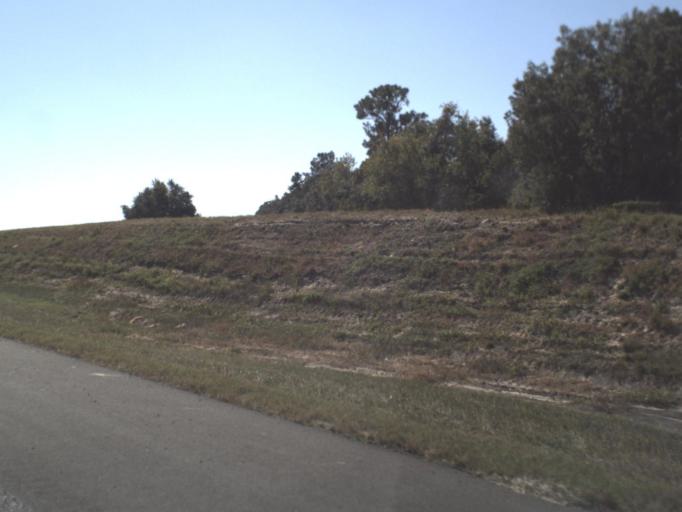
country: US
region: Florida
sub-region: Hernando County
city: Brookridge
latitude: 28.5905
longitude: -82.4839
